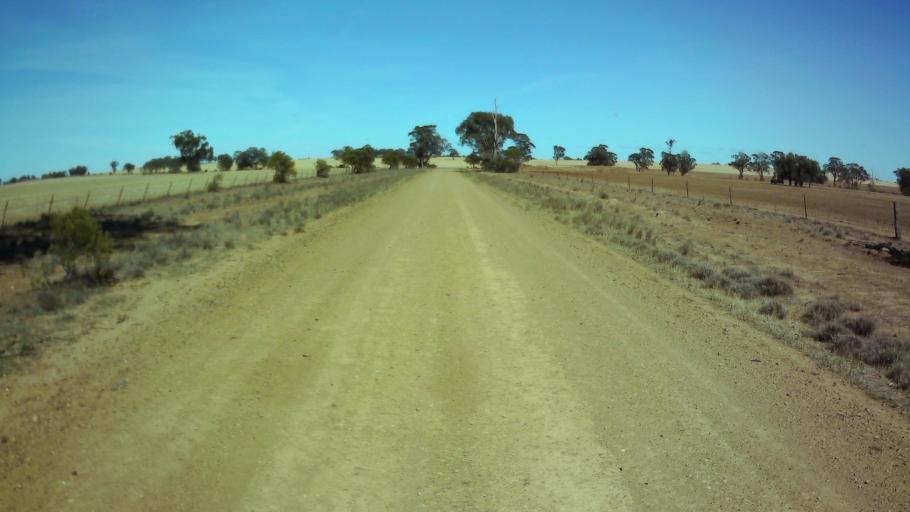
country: AU
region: New South Wales
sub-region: Weddin
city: Grenfell
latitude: -33.7484
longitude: 147.8814
